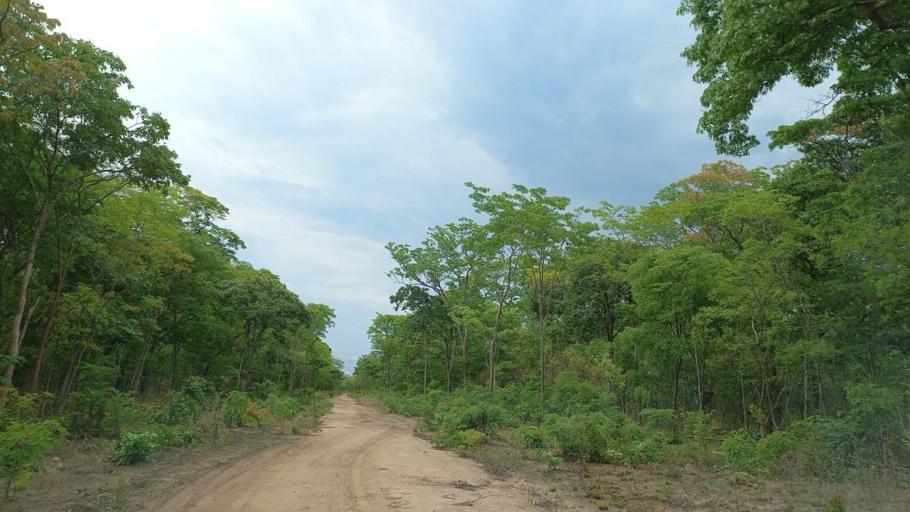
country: ZM
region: North-Western
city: Kalengwa
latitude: -13.5585
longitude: 24.9734
